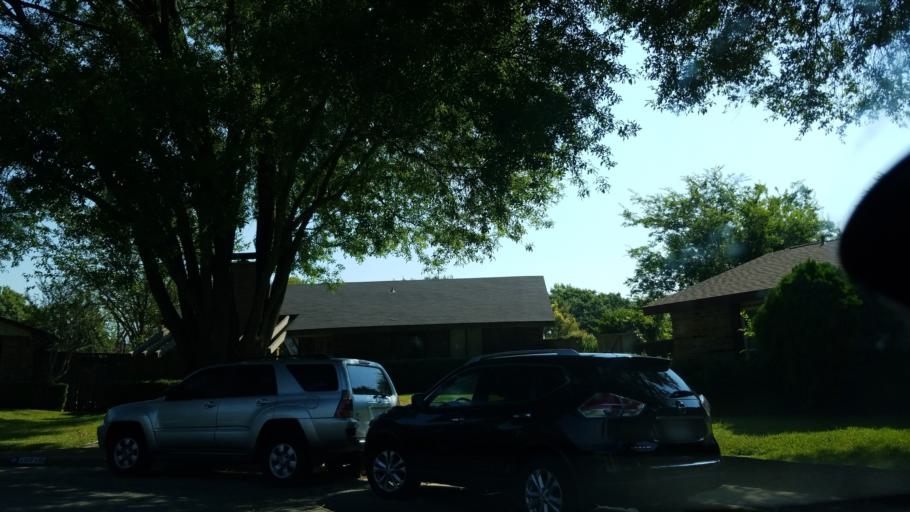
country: US
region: Texas
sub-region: Dallas County
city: Garland
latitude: 32.8735
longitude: -96.6970
